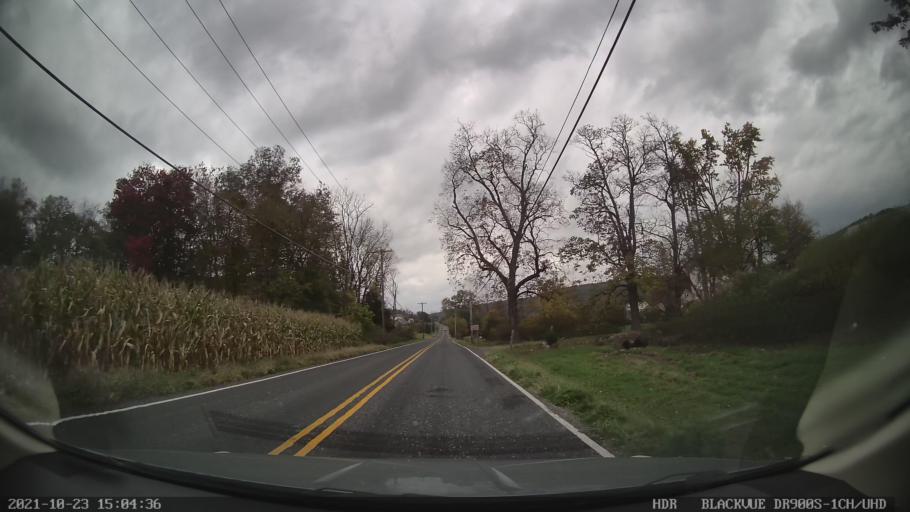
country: US
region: Pennsylvania
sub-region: Berks County
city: Bally
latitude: 40.4248
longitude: -75.5704
